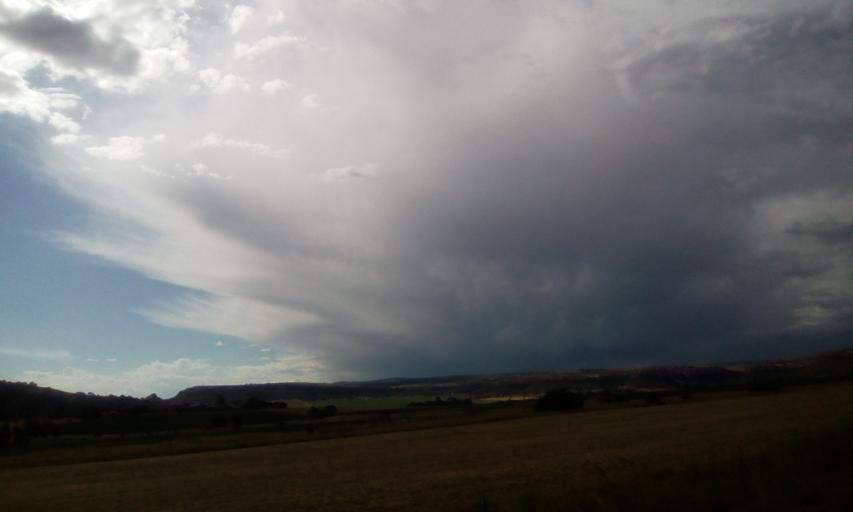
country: ZA
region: Orange Free State
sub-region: Thabo Mofutsanyana District Municipality
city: Ladybrand
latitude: -29.2534
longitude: 27.4329
